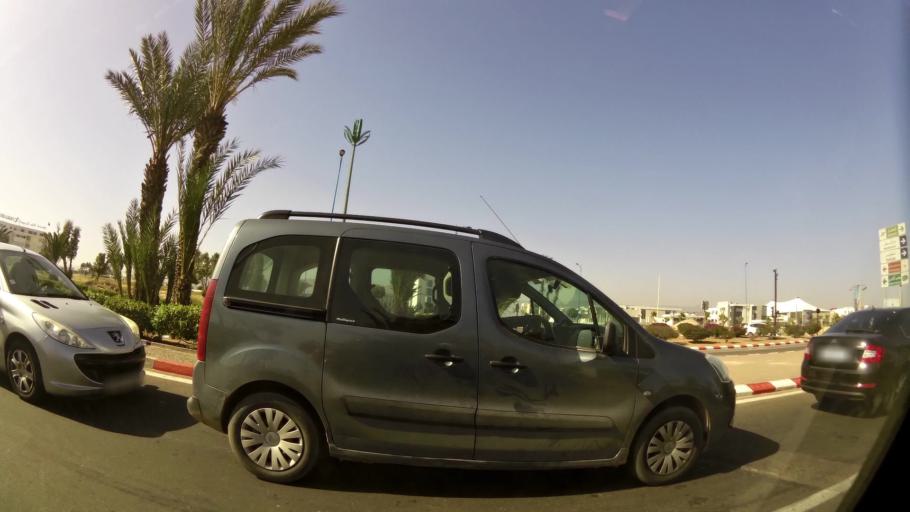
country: MA
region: Oued ed Dahab-Lagouira
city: Dakhla
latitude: 30.4045
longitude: -9.5336
